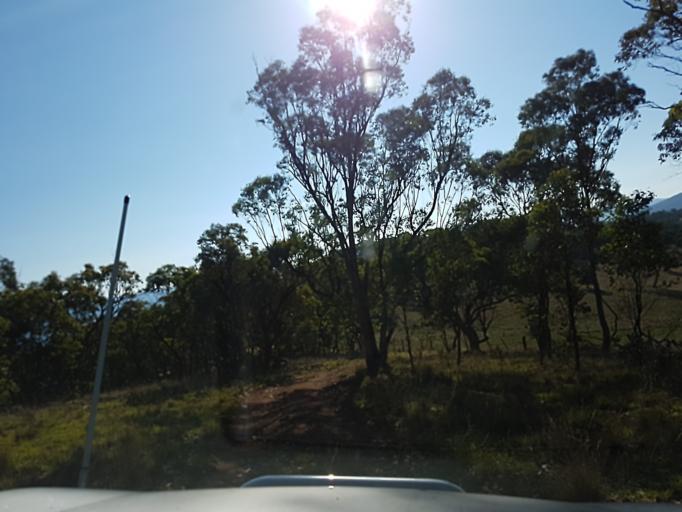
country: AU
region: New South Wales
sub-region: Snowy River
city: Jindabyne
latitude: -36.9508
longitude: 148.3504
